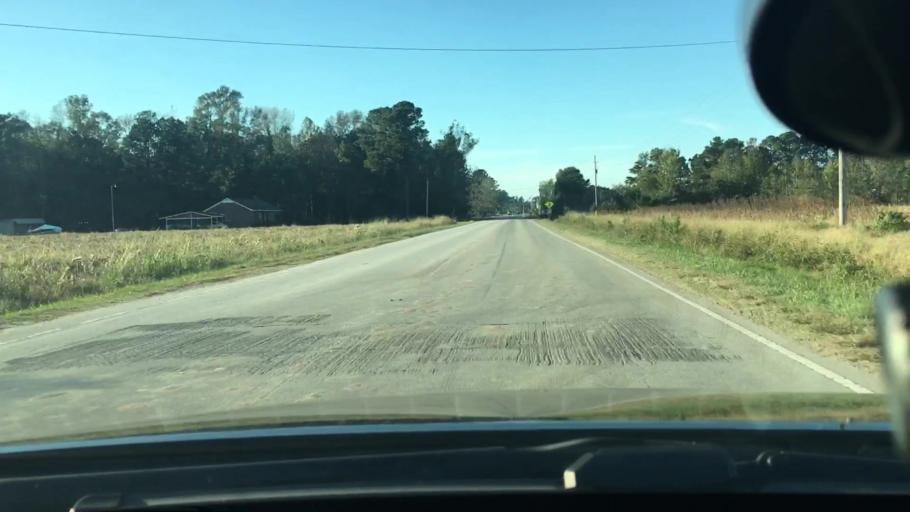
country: US
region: North Carolina
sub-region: Pitt County
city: Windsor
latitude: 35.4589
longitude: -77.2699
